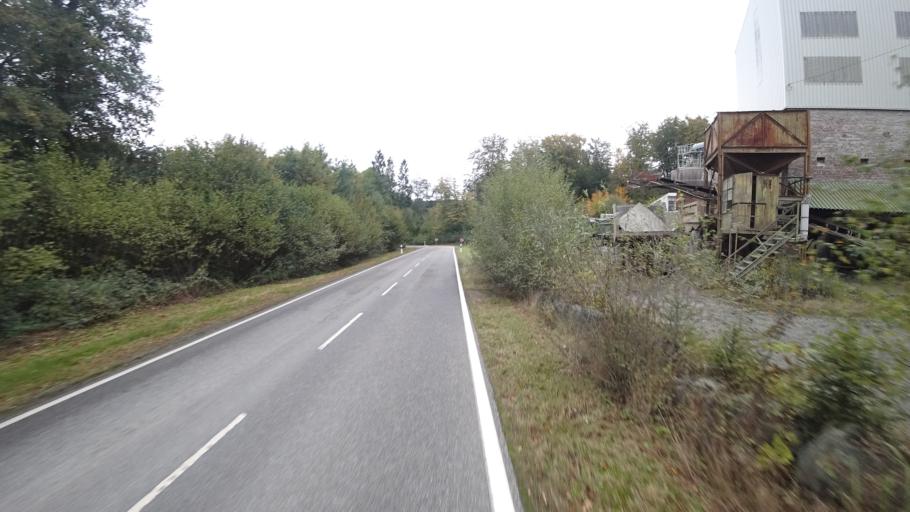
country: DE
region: Rheinland-Pfalz
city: Ruckeroth
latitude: 50.5527
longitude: 7.7618
